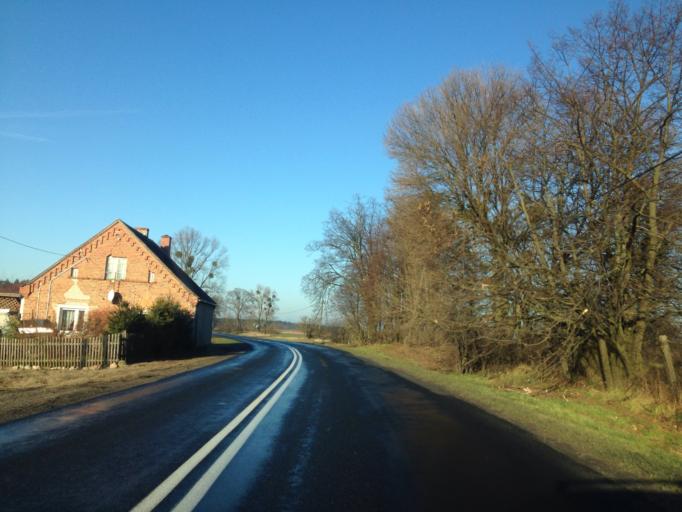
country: PL
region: Kujawsko-Pomorskie
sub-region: Powiat brodnicki
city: Bobrowo
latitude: 53.3175
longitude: 19.2757
